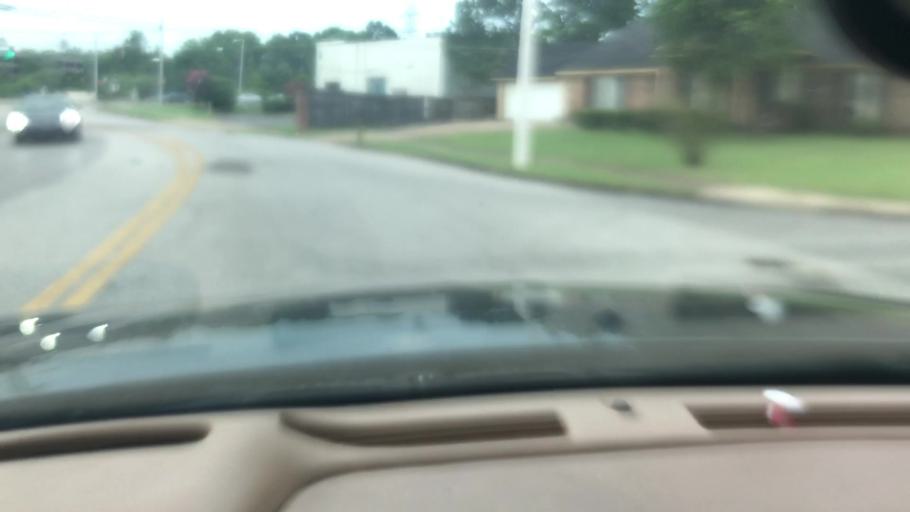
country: US
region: Tennessee
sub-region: Shelby County
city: Germantown
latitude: 35.0742
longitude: -89.8992
